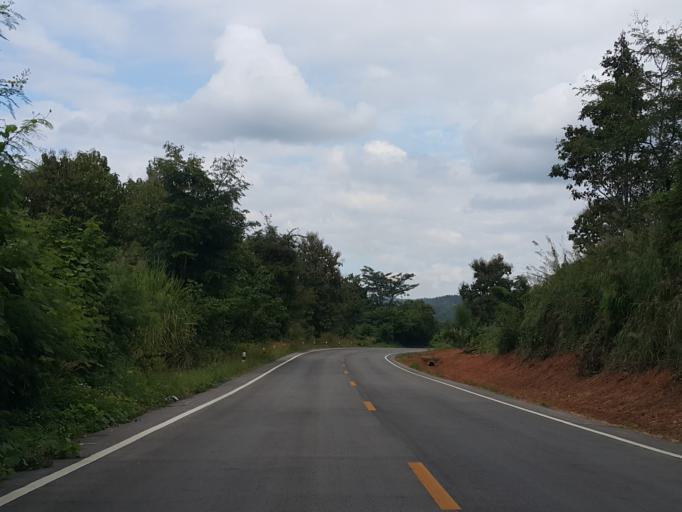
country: TH
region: Lampang
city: Chae Hom
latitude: 18.6203
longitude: 99.4828
